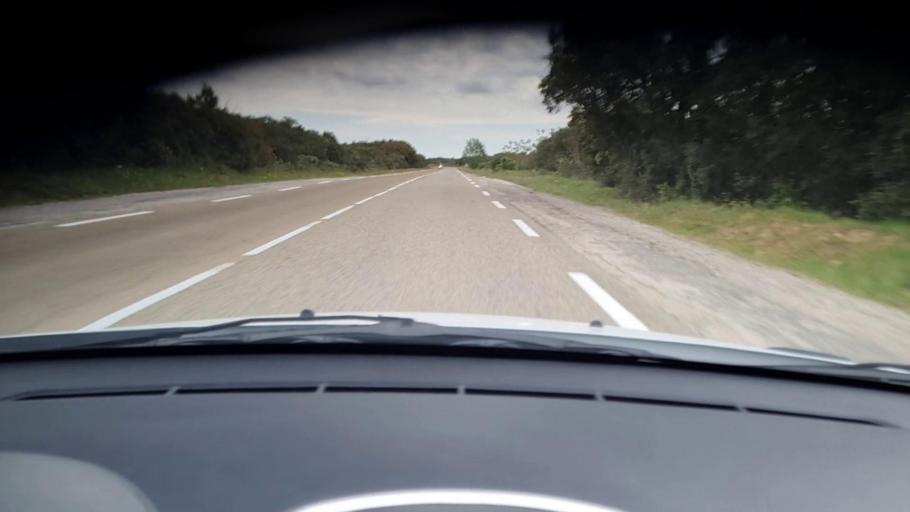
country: FR
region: Languedoc-Roussillon
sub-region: Departement du Gard
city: Poulx
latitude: 43.9076
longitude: 4.3915
